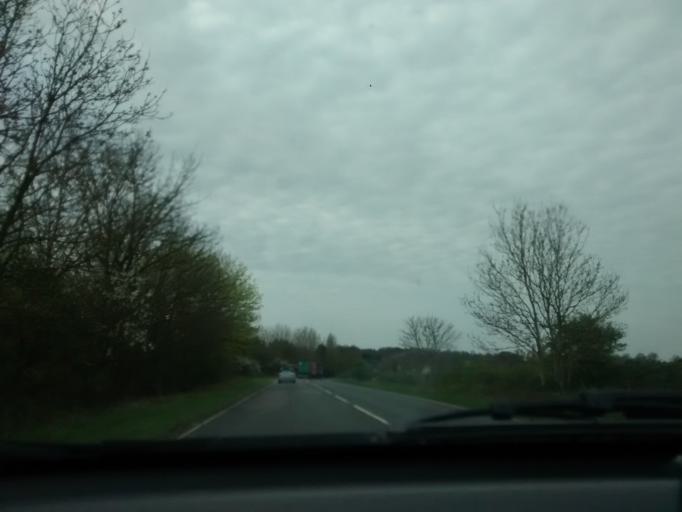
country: GB
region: England
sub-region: Oxfordshire
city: Bicester
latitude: 51.9582
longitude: -1.1042
